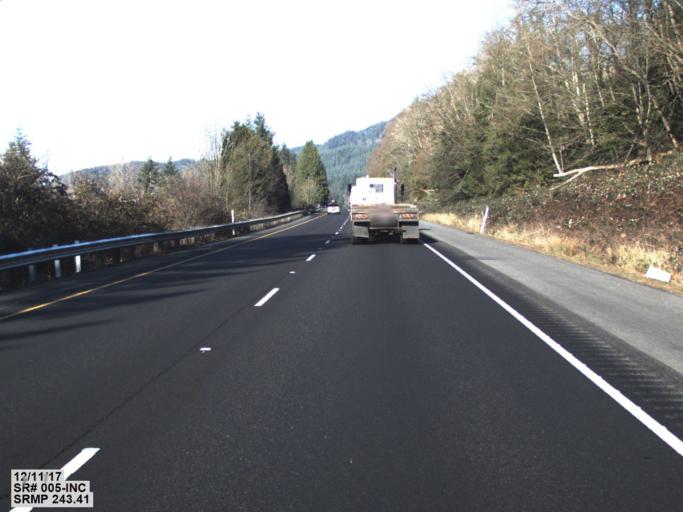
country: US
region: Washington
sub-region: Whatcom County
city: Sudden Valley
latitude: 48.6560
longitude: -122.3685
